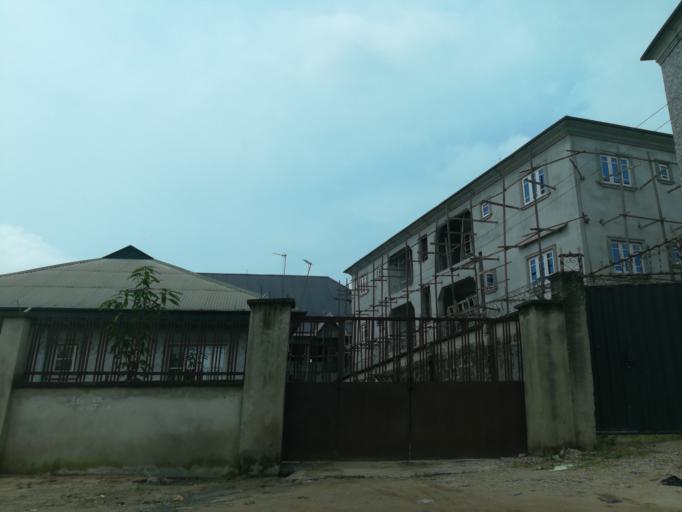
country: NG
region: Rivers
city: Port Harcourt
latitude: 4.8914
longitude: 6.9953
